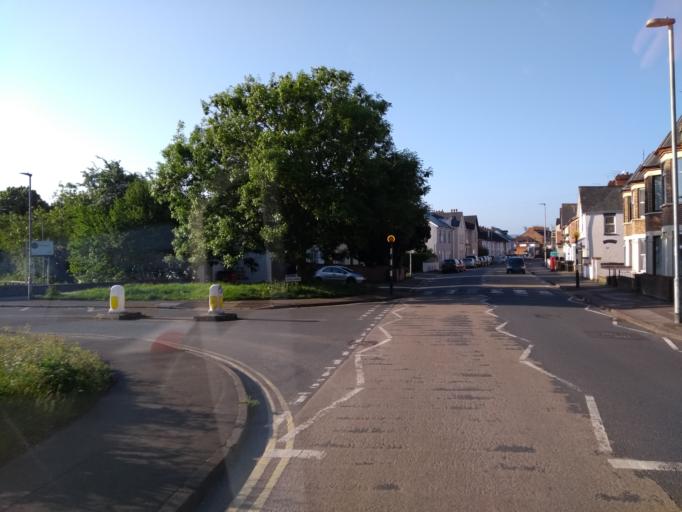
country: GB
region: England
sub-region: Somerset
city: Taunton
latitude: 51.0285
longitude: -3.1013
